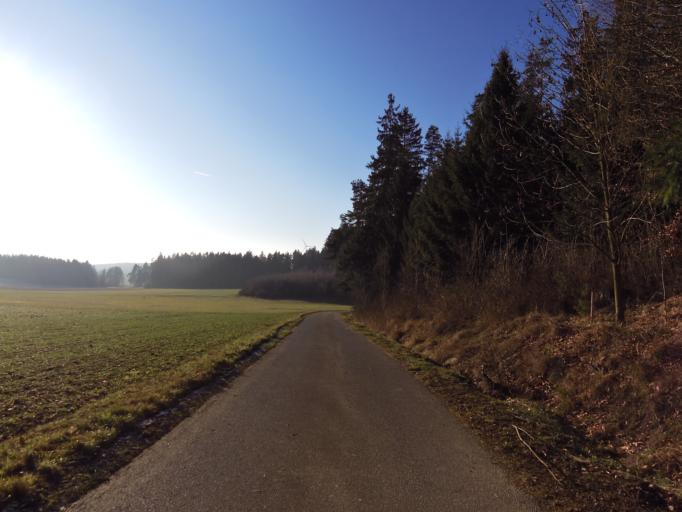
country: DE
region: Bavaria
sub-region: Upper Franconia
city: Wunsiedel
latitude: 50.0687
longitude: 12.0448
